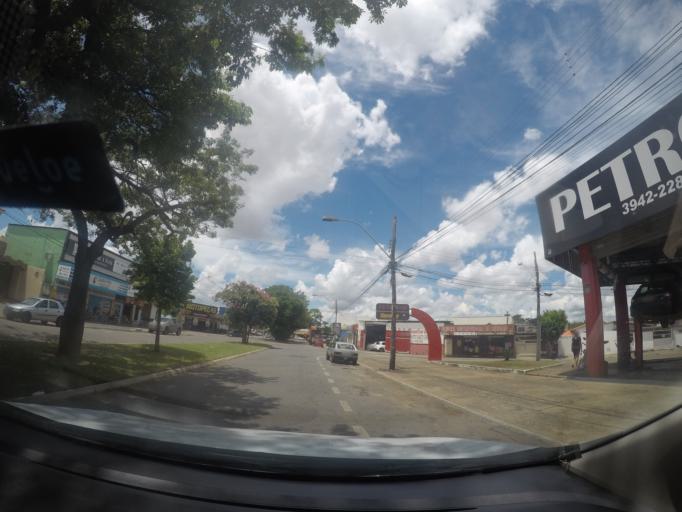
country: BR
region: Goias
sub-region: Goiania
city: Goiania
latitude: -16.6761
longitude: -49.3078
